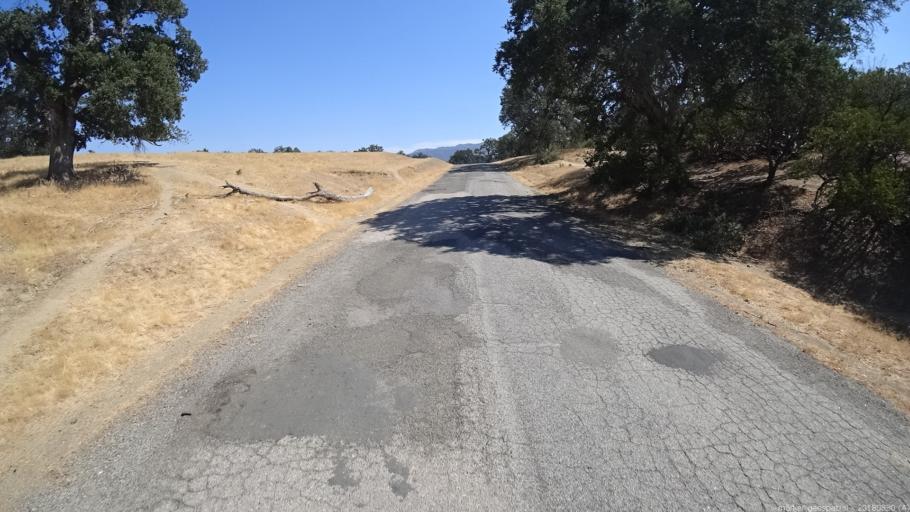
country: US
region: California
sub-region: Monterey County
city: Greenfield
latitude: 36.0863
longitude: -121.4037
